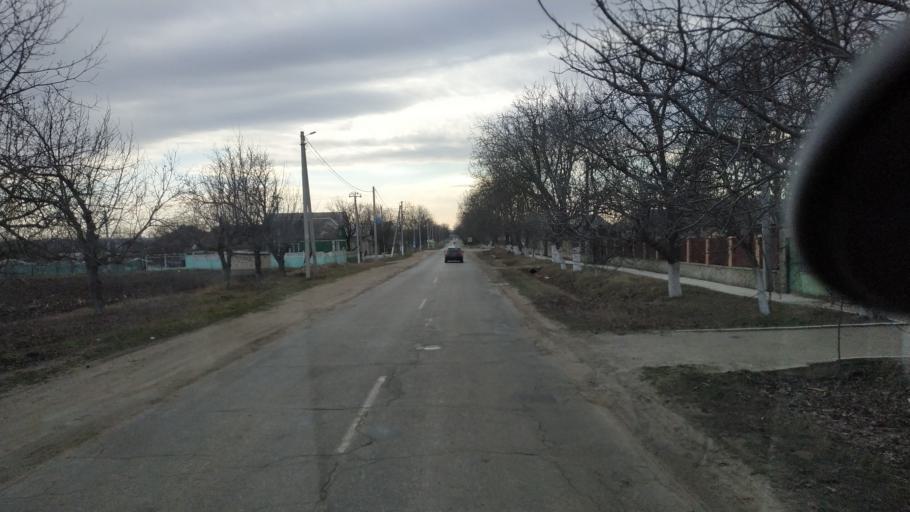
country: MD
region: Criuleni
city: Criuleni
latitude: 47.1700
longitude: 29.1265
